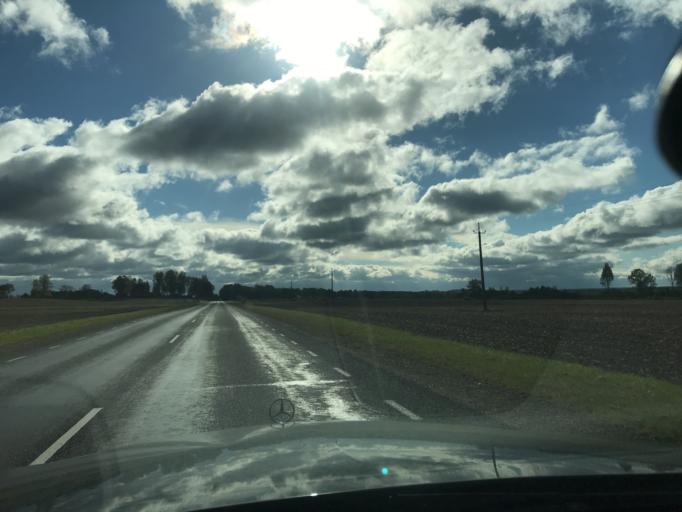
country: EE
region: Valgamaa
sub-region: Valga linn
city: Valga
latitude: 57.9695
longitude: 26.2628
